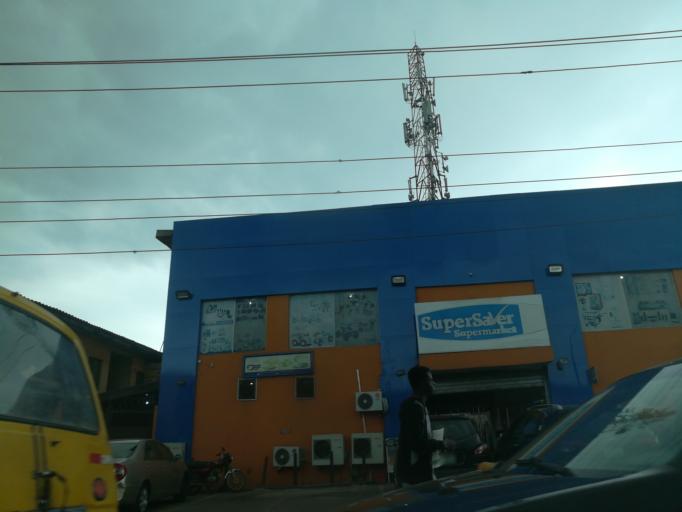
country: NG
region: Lagos
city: Ojota
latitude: 6.5998
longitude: 3.3815
